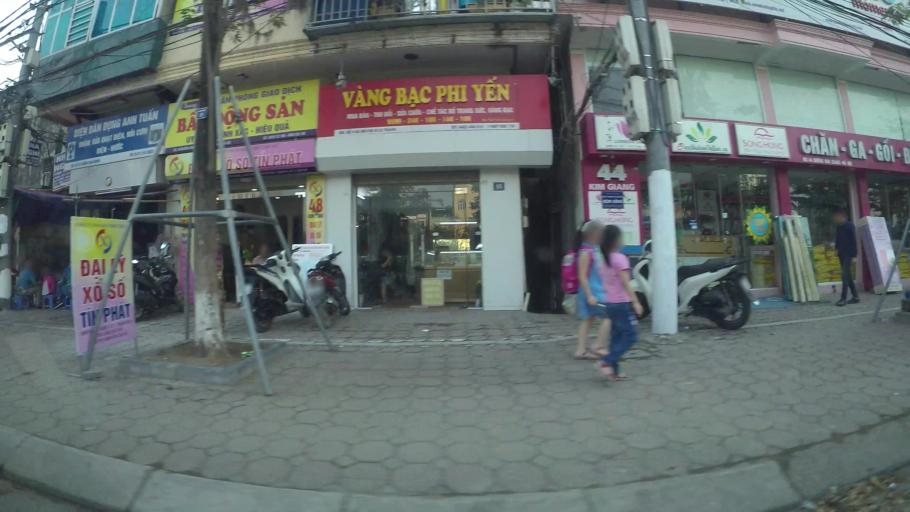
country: VN
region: Ha Noi
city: Thanh Xuan
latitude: 20.9844
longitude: 105.8145
